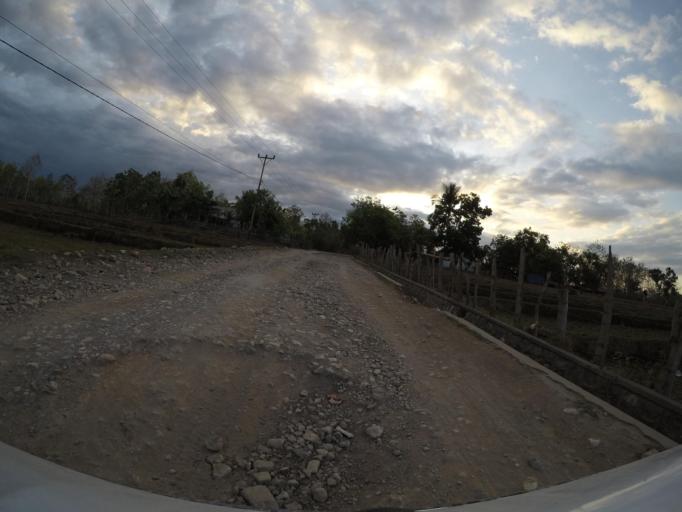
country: TL
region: Bobonaro
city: Maliana
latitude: -8.9235
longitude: 125.2120
